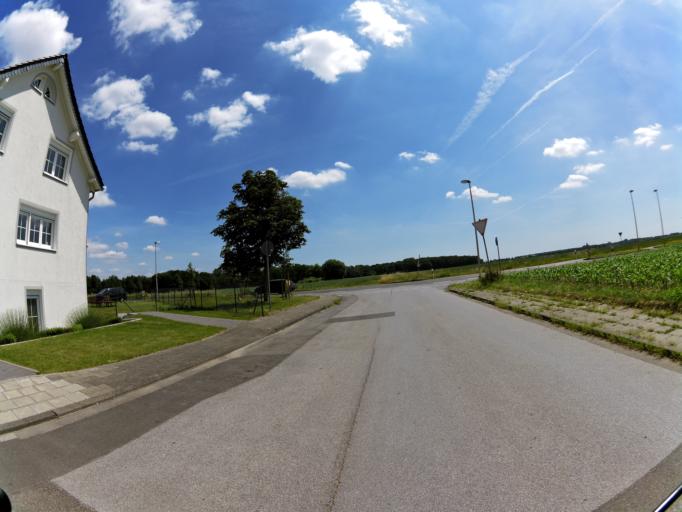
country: DE
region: North Rhine-Westphalia
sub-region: Regierungsbezirk Koln
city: Selfkant
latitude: 51.0331
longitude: 5.9079
